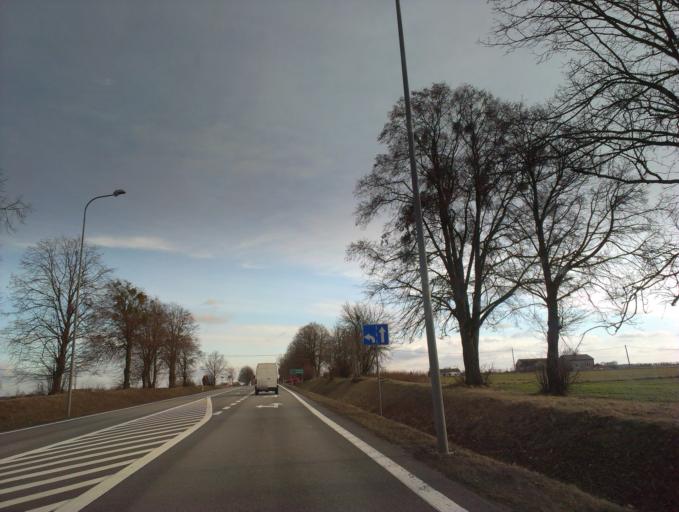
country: PL
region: Kujawsko-Pomorskie
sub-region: Powiat lipnowski
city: Kikol
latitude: 52.9329
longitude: 19.0639
